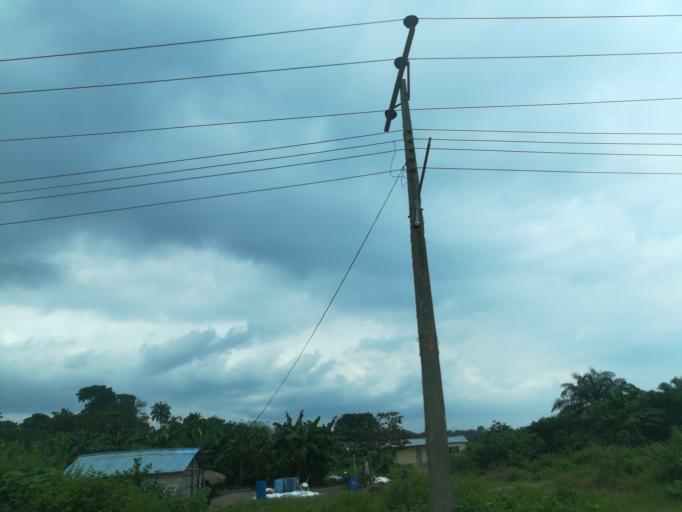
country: NG
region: Lagos
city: Ejirin
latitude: 6.6479
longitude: 3.8319
